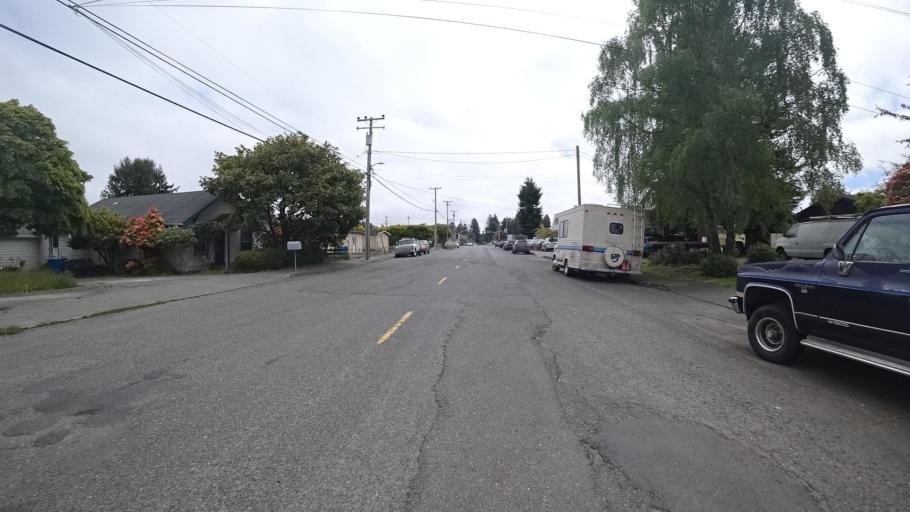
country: US
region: California
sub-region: Humboldt County
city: Cutten
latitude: 40.7698
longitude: -124.1448
